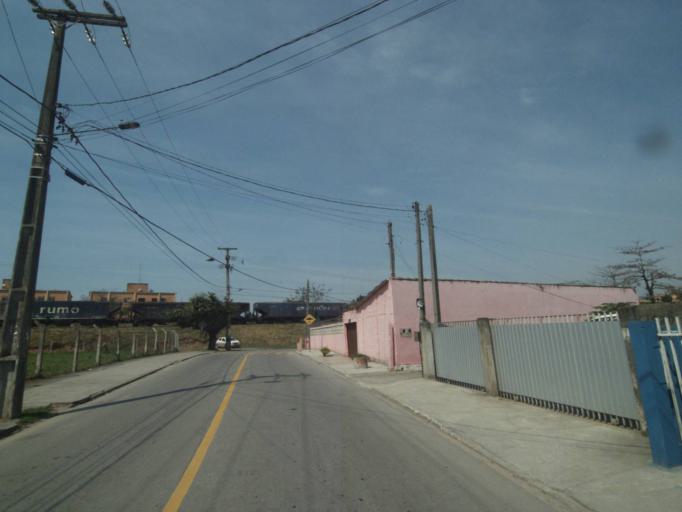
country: BR
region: Parana
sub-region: Paranagua
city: Paranagua
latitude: -25.5470
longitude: -48.5521
